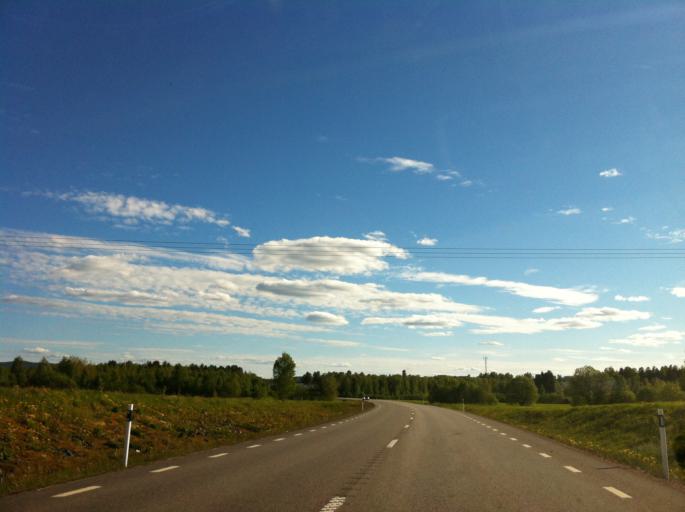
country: SE
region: Dalarna
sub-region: Leksand Municipality
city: Leksand
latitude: 60.7443
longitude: 15.0113
